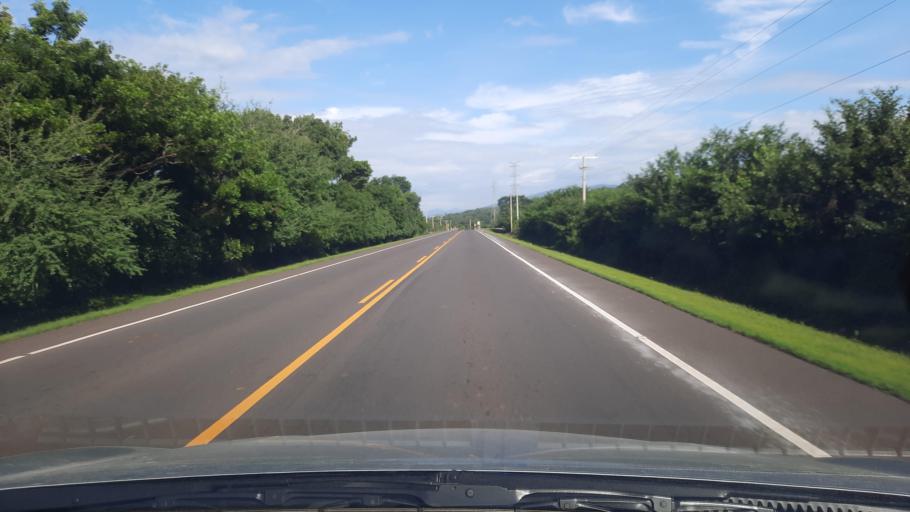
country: NI
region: Chinandega
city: Chichigalpa
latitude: 12.7419
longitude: -86.8911
